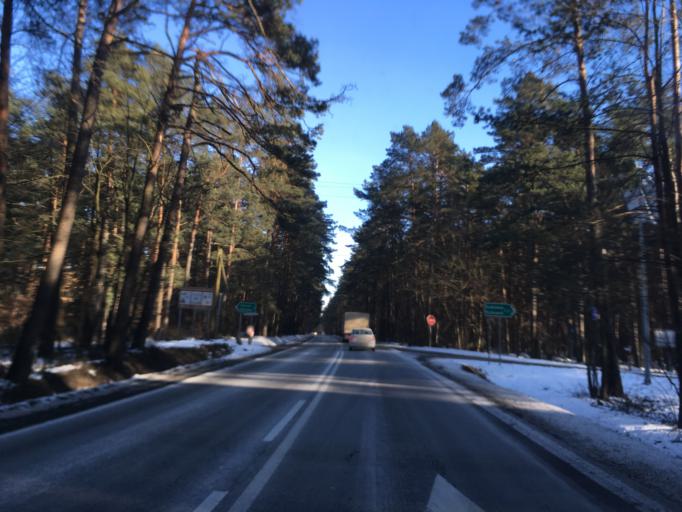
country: PL
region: Pomeranian Voivodeship
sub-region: Powiat koscierski
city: Koscierzyna
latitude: 54.1149
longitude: 17.9001
